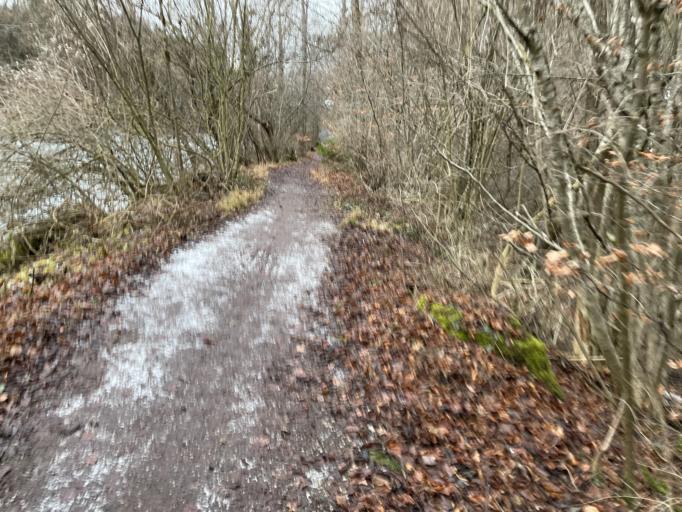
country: CH
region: Bern
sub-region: Thun District
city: Uttigen
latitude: 46.8027
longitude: 7.5696
